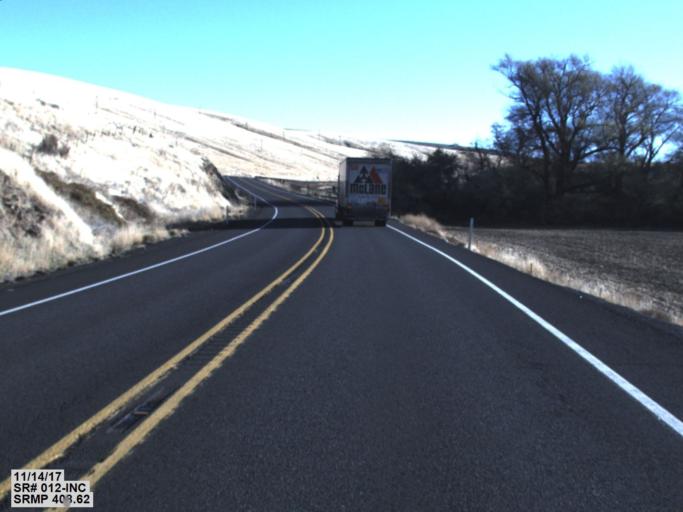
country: US
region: Washington
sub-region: Garfield County
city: Pomeroy
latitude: 46.4673
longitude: -117.4941
